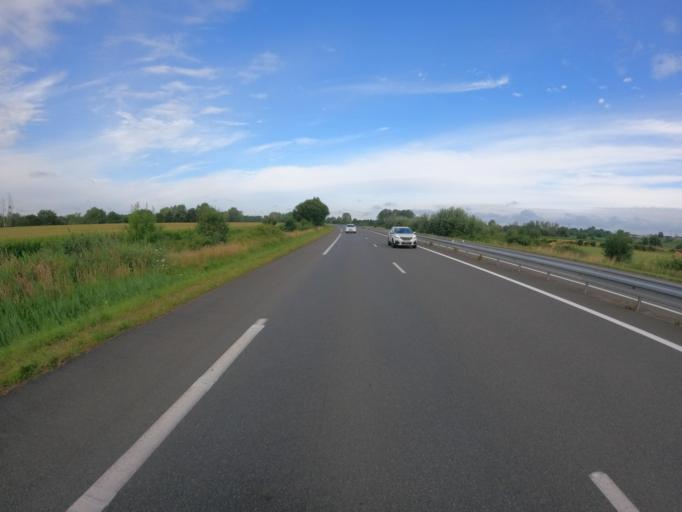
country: FR
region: Centre
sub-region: Departement d'Indre-et-Loire
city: Saint-Nicolas-de-Bourgueil
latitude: 47.2758
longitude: 0.0980
